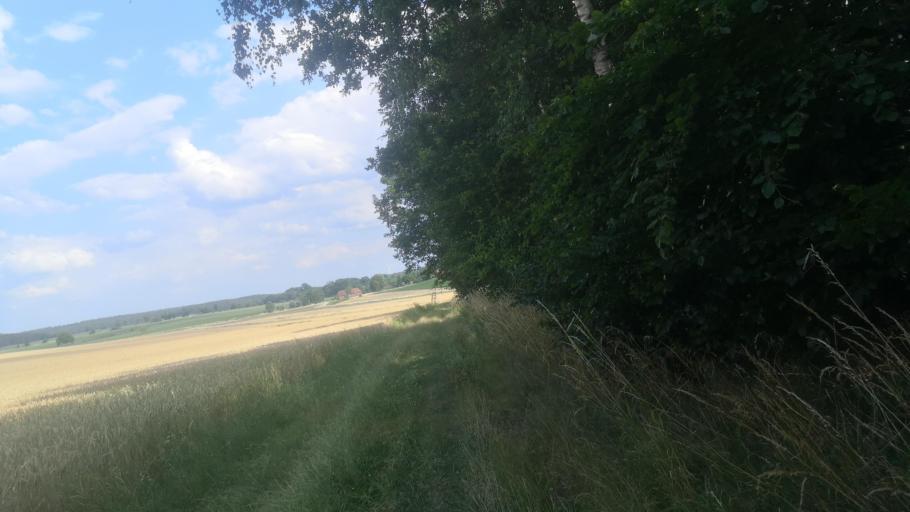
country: DE
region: Lower Saxony
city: Dahlem
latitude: 53.2201
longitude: 10.7466
